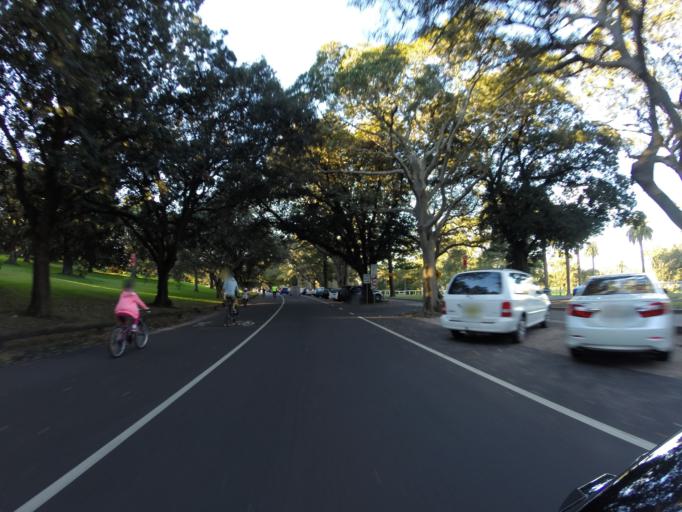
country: AU
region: New South Wales
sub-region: Woollahra
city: Woollahra
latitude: -33.8968
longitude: 151.2301
